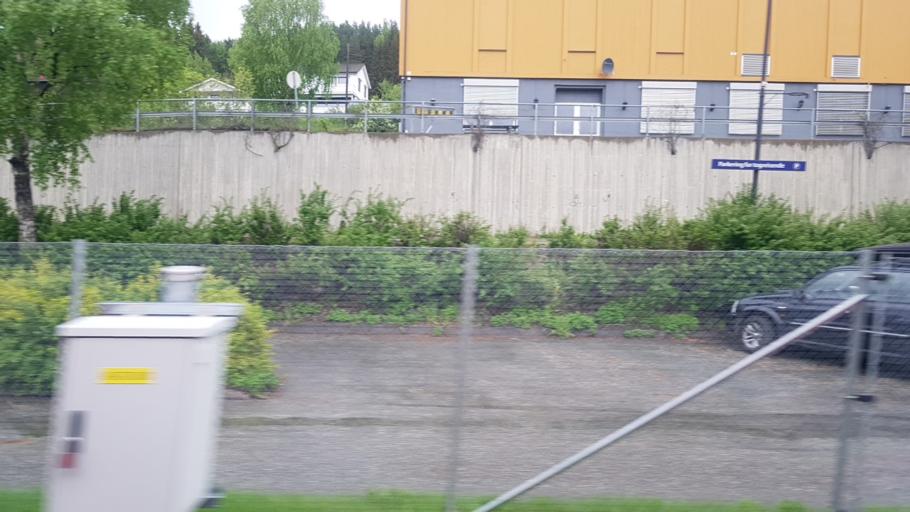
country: NO
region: Oppland
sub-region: Nord-Fron
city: Vinstra
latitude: 61.5966
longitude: 9.7341
